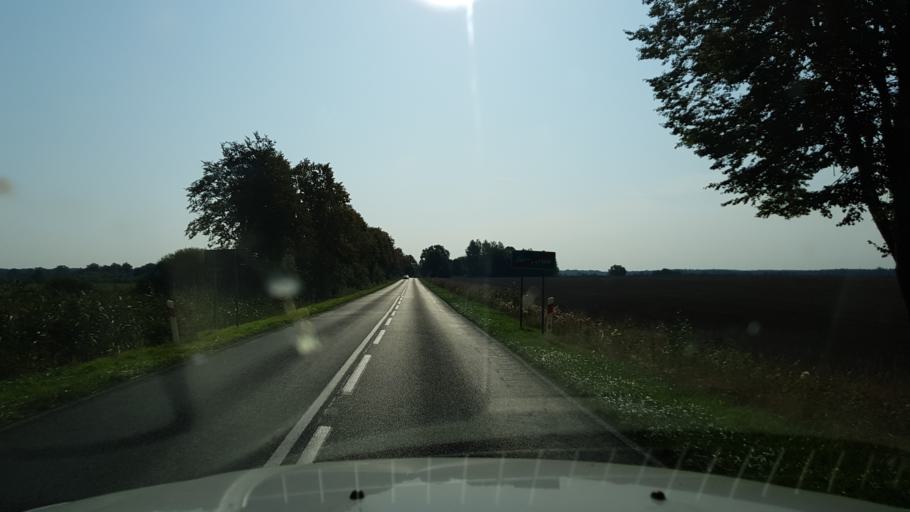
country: PL
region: West Pomeranian Voivodeship
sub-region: Powiat gryficki
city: Ploty
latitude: 53.7901
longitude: 15.2996
